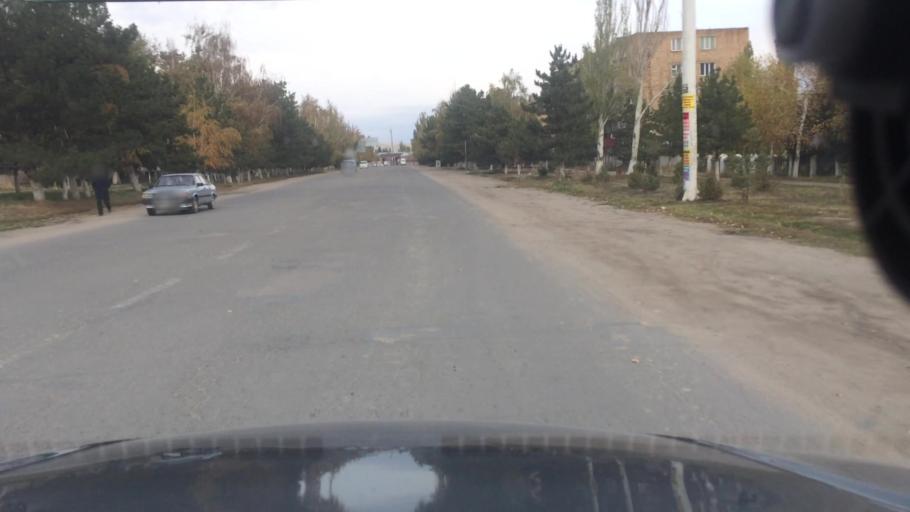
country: KG
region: Ysyk-Koel
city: Karakol
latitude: 42.4968
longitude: 78.3907
